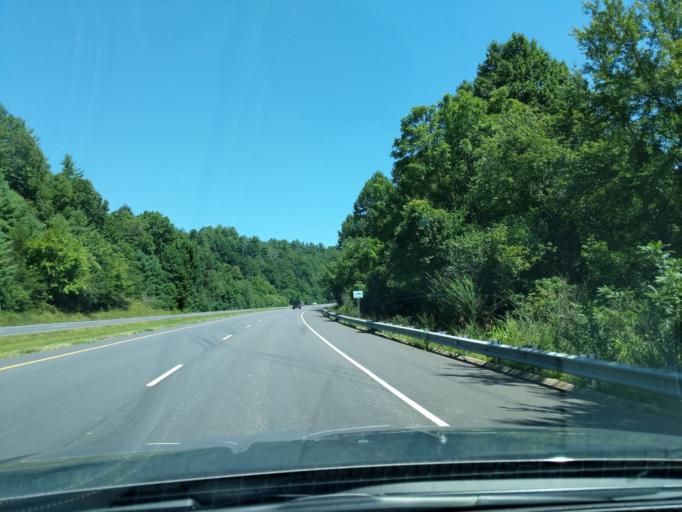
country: US
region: North Carolina
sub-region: Macon County
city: Franklin
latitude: 35.1541
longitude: -83.4640
